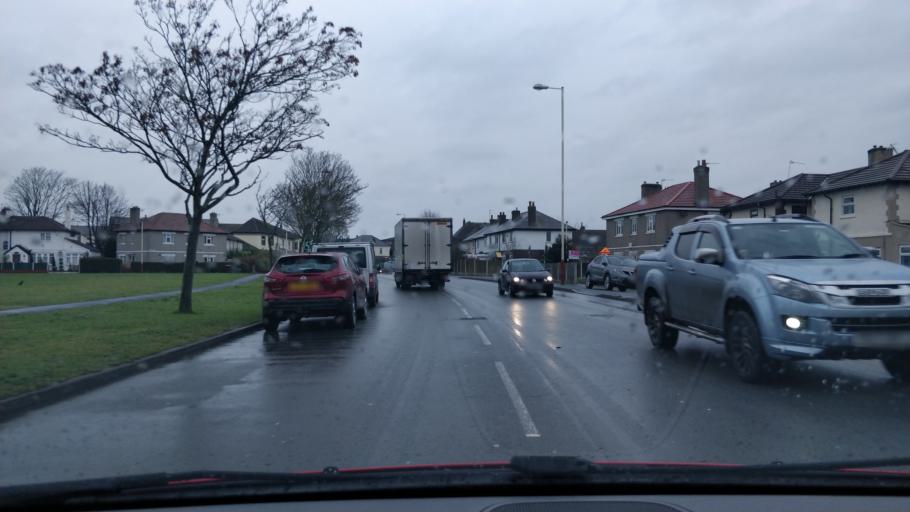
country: GB
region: England
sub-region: Sefton
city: Southport
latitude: 53.6013
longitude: -3.0331
